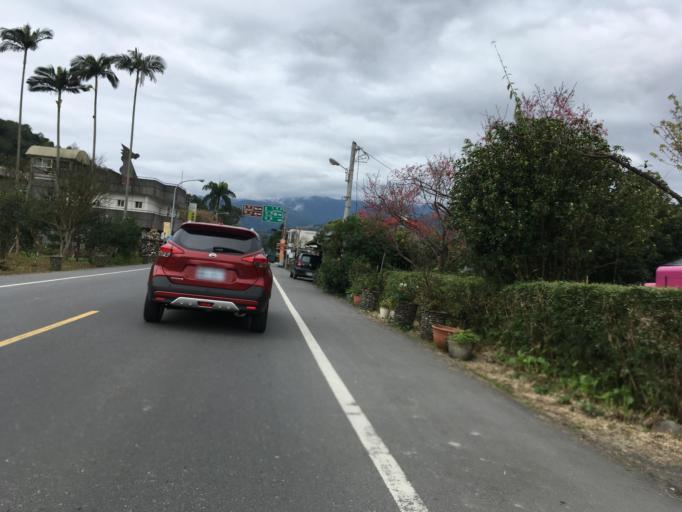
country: TW
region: Taiwan
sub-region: Yilan
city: Yilan
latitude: 24.6617
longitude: 121.6198
